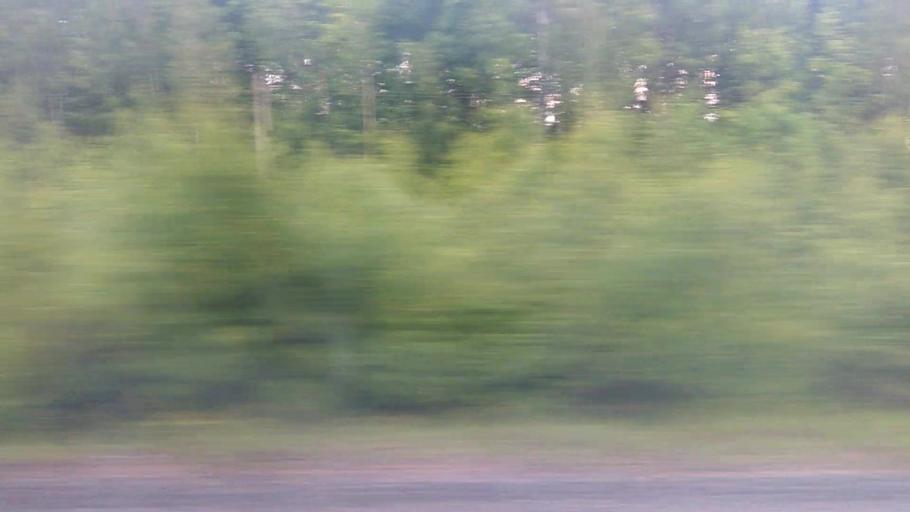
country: RU
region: Moskovskaya
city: Mikhnevo
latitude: 55.0805
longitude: 37.9755
